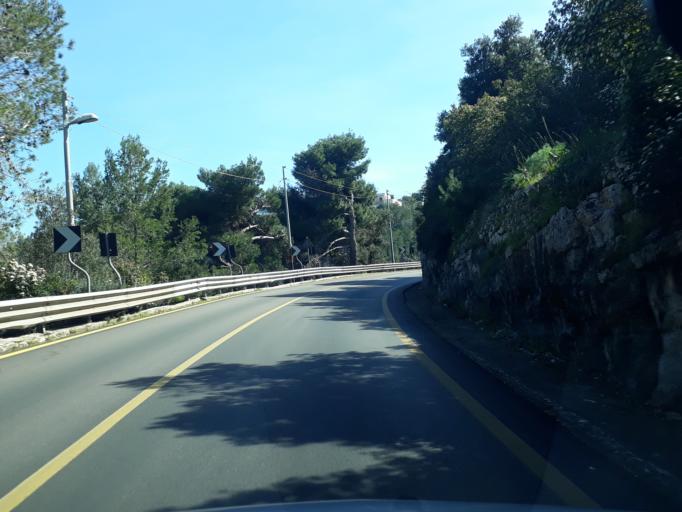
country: IT
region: Apulia
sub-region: Provincia di Brindisi
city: Lamie di Olimpie-Selva
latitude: 40.8050
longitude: 17.3505
